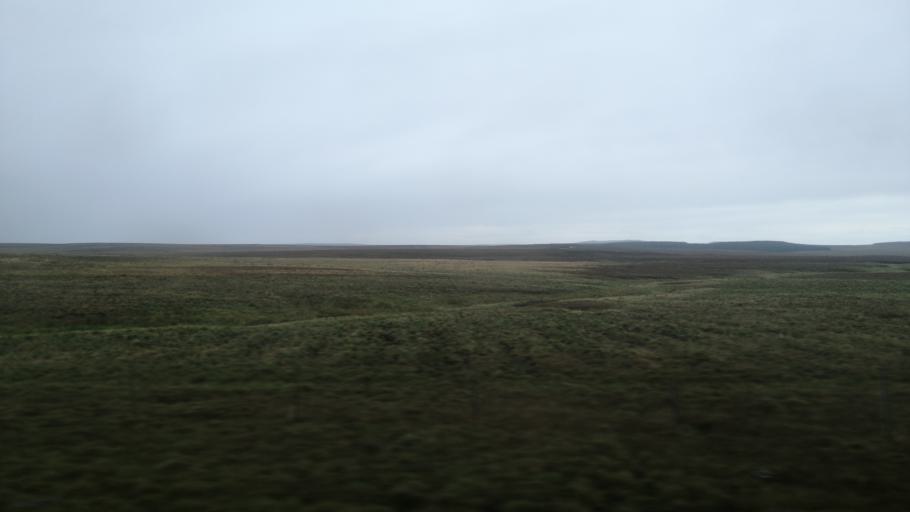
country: GB
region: Scotland
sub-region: Highland
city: Thurso
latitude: 58.3698
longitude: -3.7508
